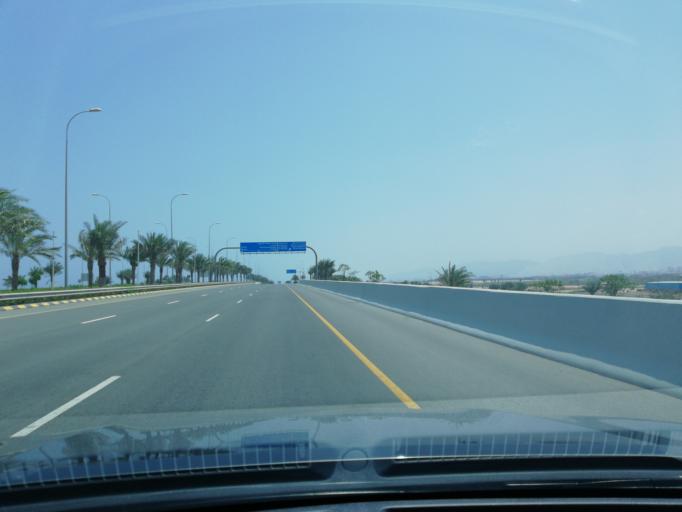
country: OM
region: Muhafazat Masqat
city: Bawshar
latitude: 23.6026
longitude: 58.3088
